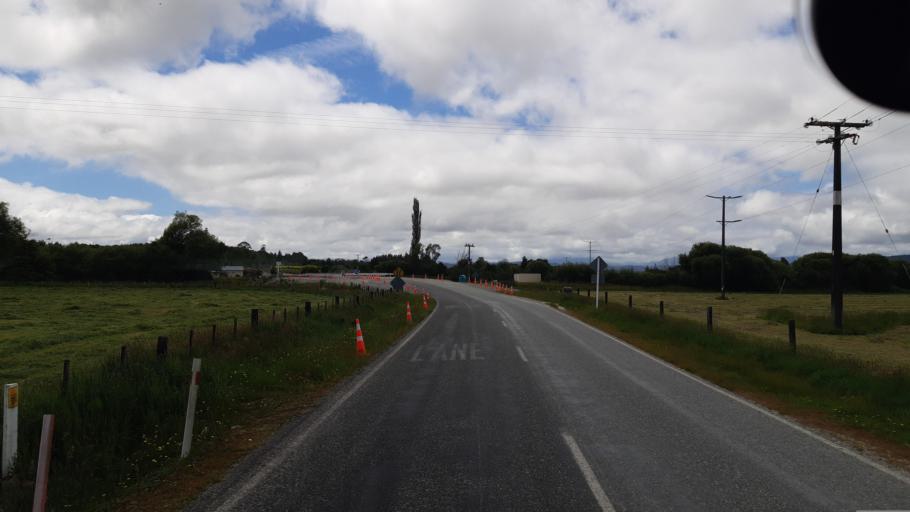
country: NZ
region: West Coast
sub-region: Grey District
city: Greymouth
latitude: -42.3377
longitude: 171.4738
